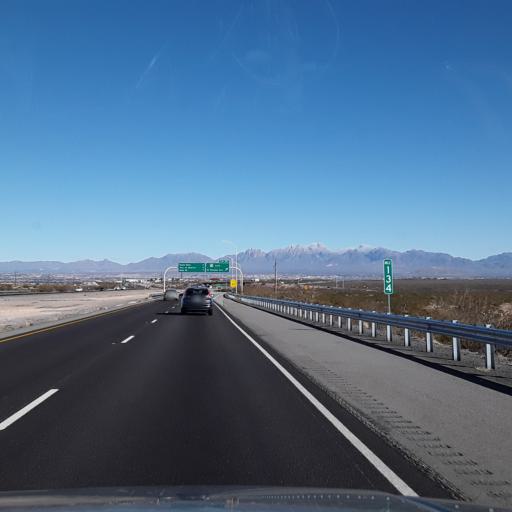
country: US
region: New Mexico
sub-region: Dona Ana County
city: Mesilla
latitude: 32.2792
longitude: -106.8919
